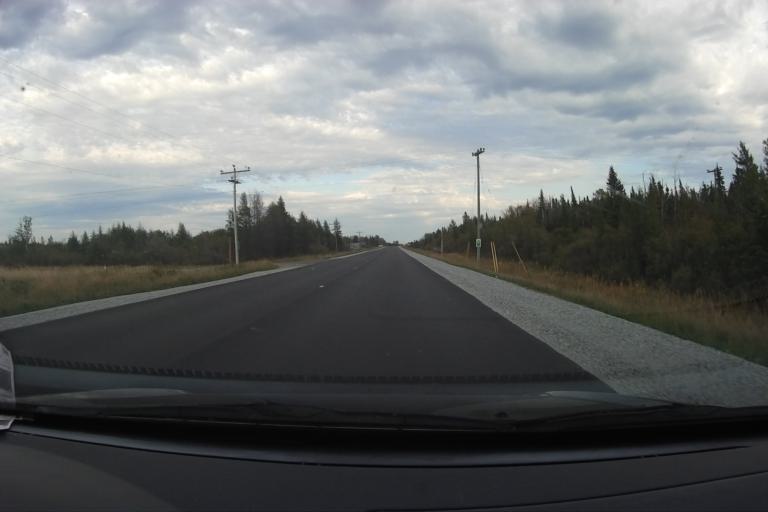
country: CA
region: Ontario
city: Hearst
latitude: 49.6712
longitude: -83.5217
